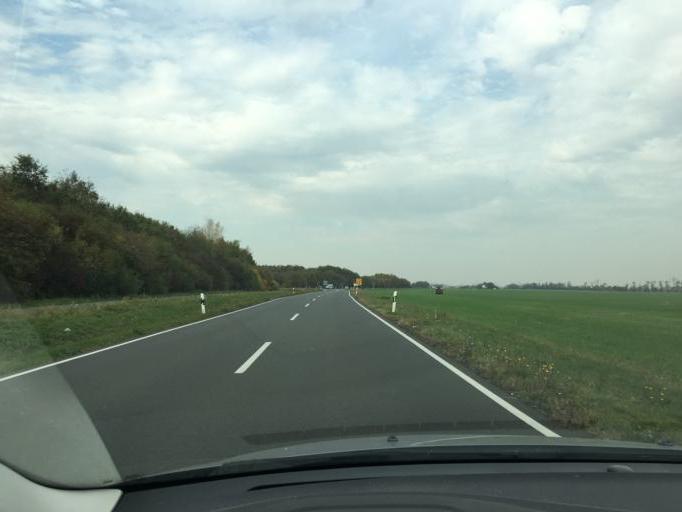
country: DE
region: Saxony
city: Zwochau
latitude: 51.4384
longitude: 12.2771
